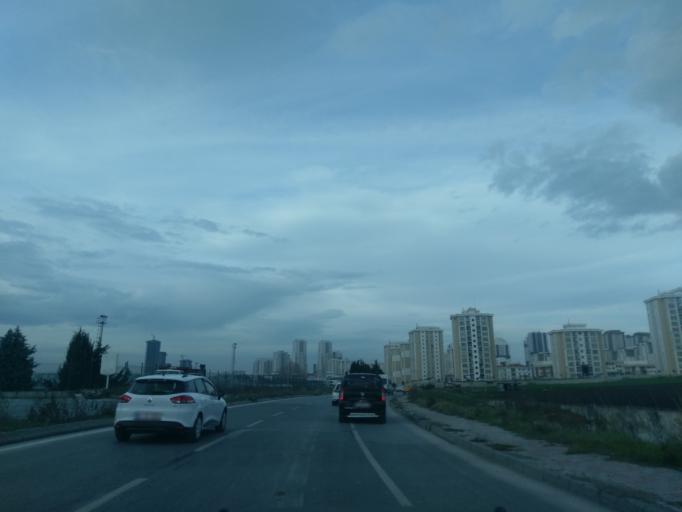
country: TR
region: Istanbul
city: Esenyurt
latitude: 41.0803
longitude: 28.6530
